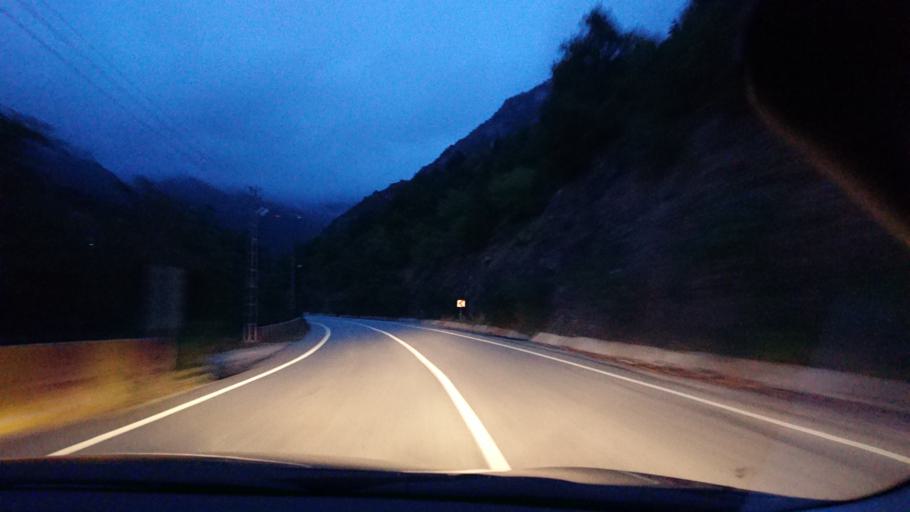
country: TR
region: Gumushane
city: Kurtun
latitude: 40.6746
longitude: 39.1396
